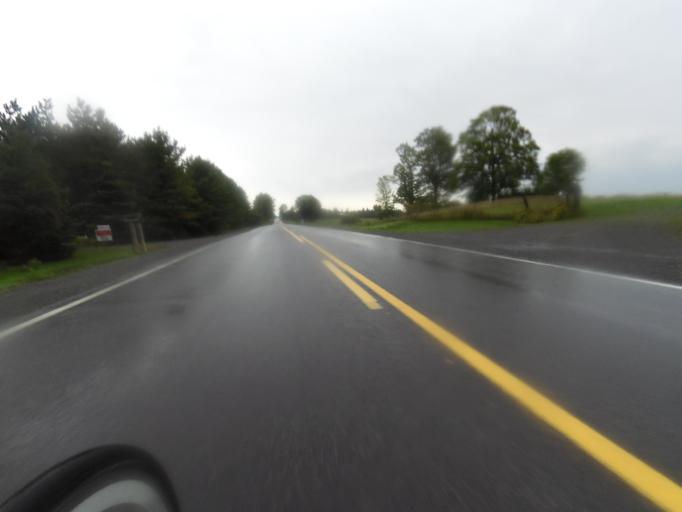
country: CA
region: Ontario
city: Bells Corners
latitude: 45.1832
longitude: -75.6715
